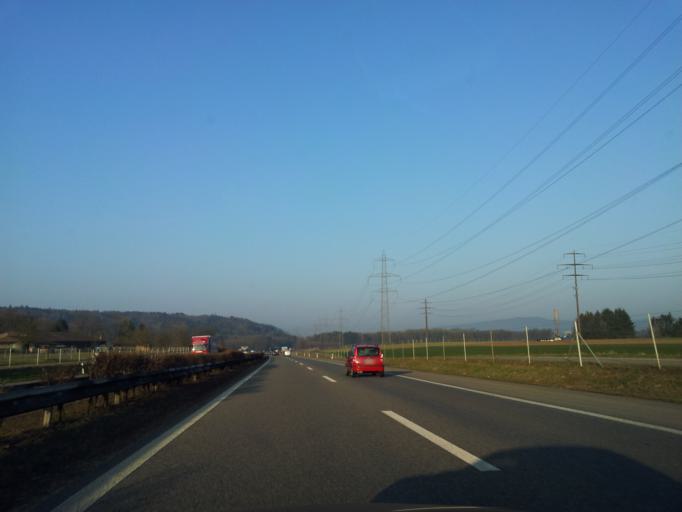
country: CH
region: Aargau
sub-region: Bezirk Rheinfelden
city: Mohlin
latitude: 47.5469
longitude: 7.8320
